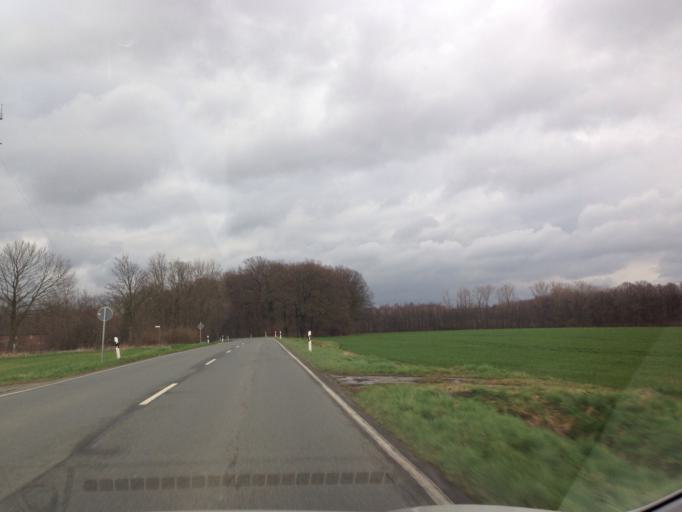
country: DE
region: North Rhine-Westphalia
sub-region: Regierungsbezirk Munster
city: Nordkirchen
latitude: 51.7598
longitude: 7.5263
